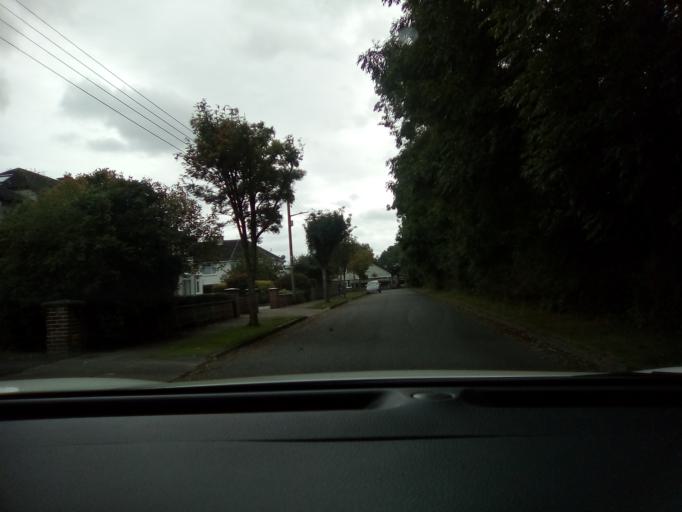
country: IE
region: Leinster
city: Lucan
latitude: 53.3564
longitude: -6.4693
